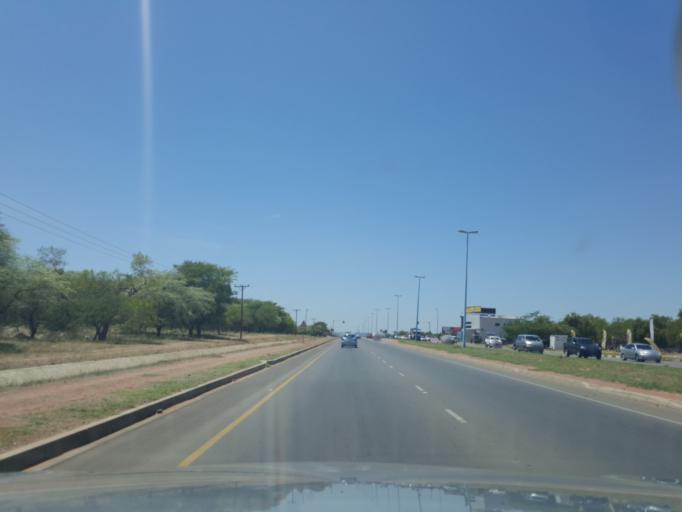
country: BW
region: Kweneng
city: Mogoditshane
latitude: -24.6049
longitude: 25.8566
